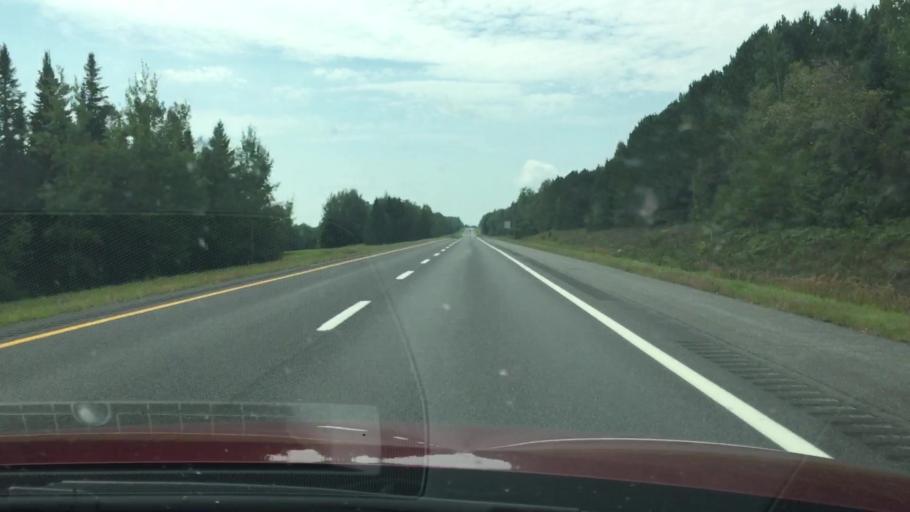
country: US
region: Maine
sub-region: Aroostook County
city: Hodgdon
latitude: 46.1333
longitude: -68.0886
